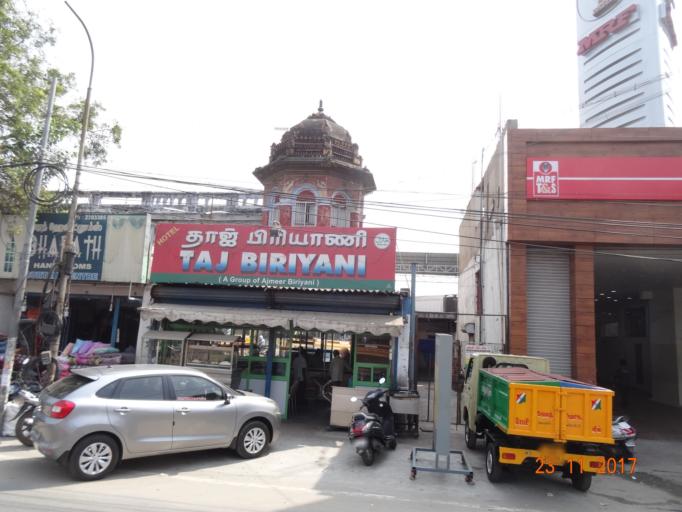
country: IN
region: Tamil Nadu
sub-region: Coimbatore
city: Coimbatore
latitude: 10.9942
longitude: 76.9658
